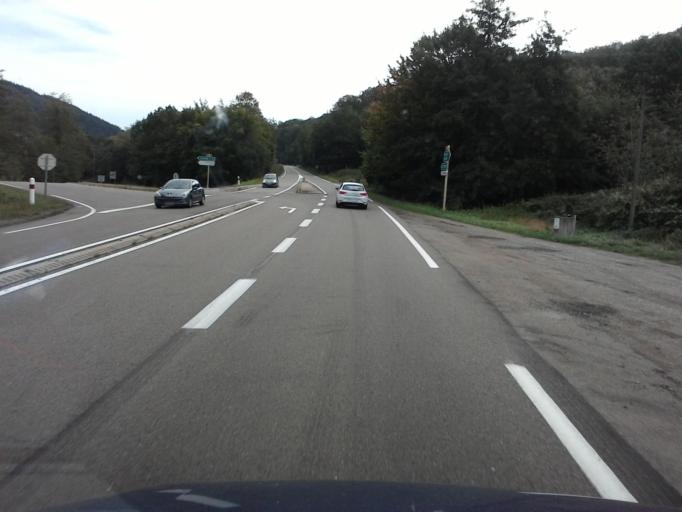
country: FR
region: Bourgogne
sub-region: Departement de Saone-et-Loire
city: Autun
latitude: 46.9481
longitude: 4.3429
